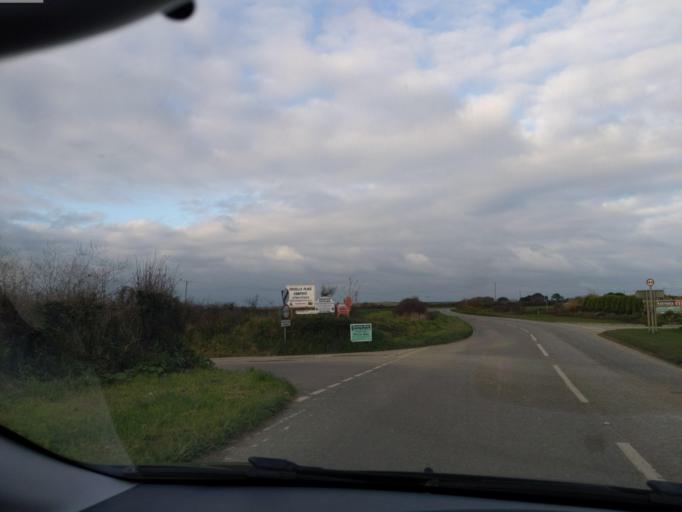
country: GB
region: England
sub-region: Cornwall
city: Padstow
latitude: 50.5253
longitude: -4.9534
